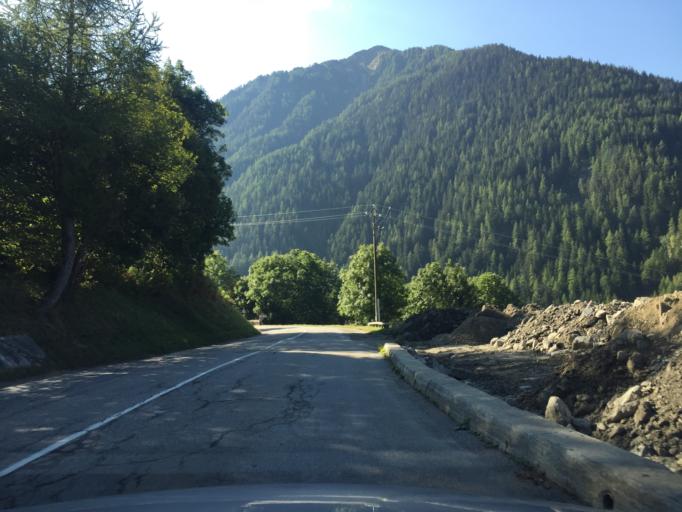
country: FR
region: Rhone-Alpes
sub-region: Departement de la Savoie
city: Belle-Plagne
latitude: 45.5427
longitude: 6.7579
